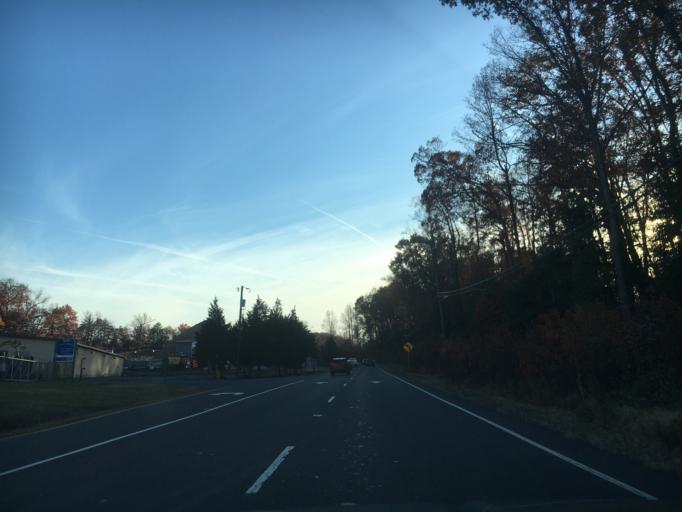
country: US
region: Virginia
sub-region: Prince William County
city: Dumfries
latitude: 38.5582
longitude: -77.3337
